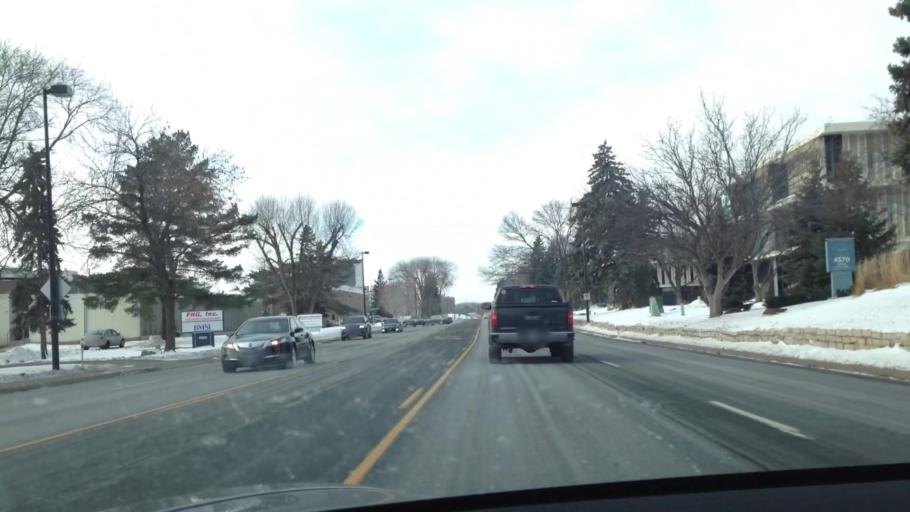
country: US
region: Minnesota
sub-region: Hennepin County
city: Edina
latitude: 44.8632
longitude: -93.3385
